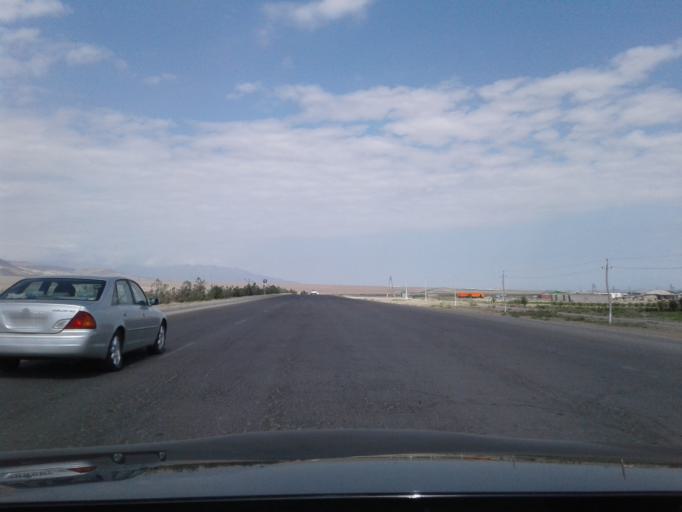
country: TM
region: Ahal
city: Baharly
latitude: 38.4437
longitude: 57.3851
